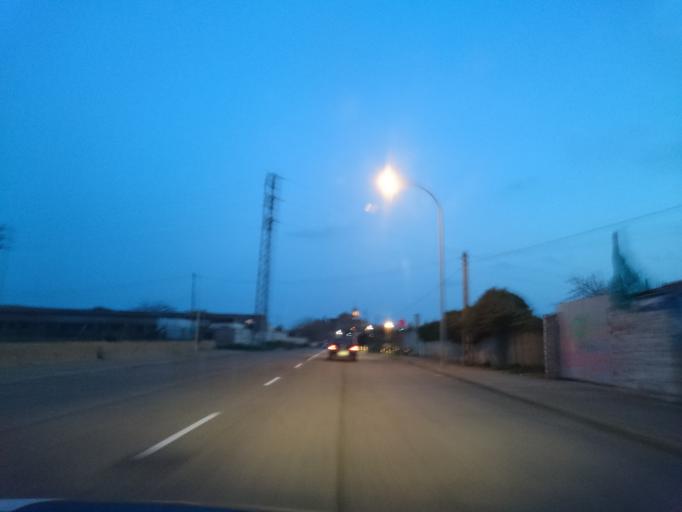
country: ES
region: Catalonia
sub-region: Provincia de Barcelona
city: Vilanova i la Geltru
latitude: 41.2319
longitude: 1.7212
